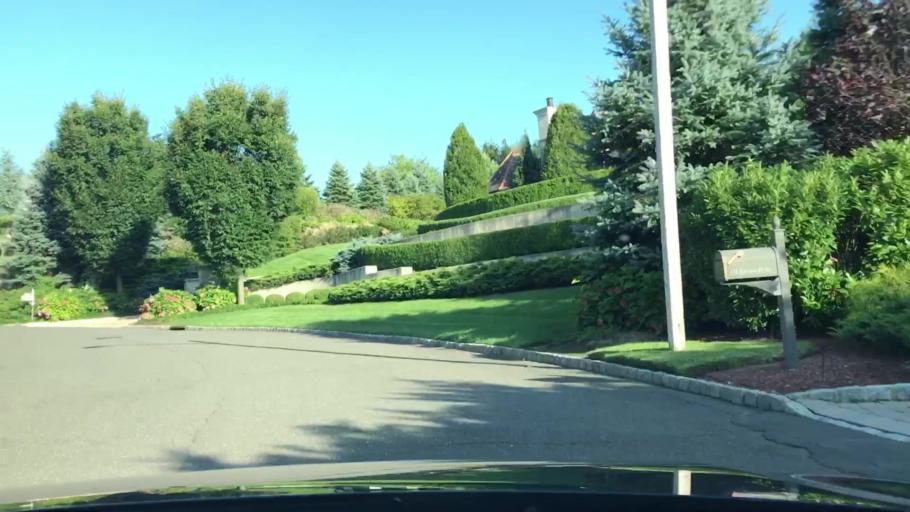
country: US
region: New Jersey
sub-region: Bergen County
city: Tenafly
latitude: 40.9273
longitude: -73.9429
